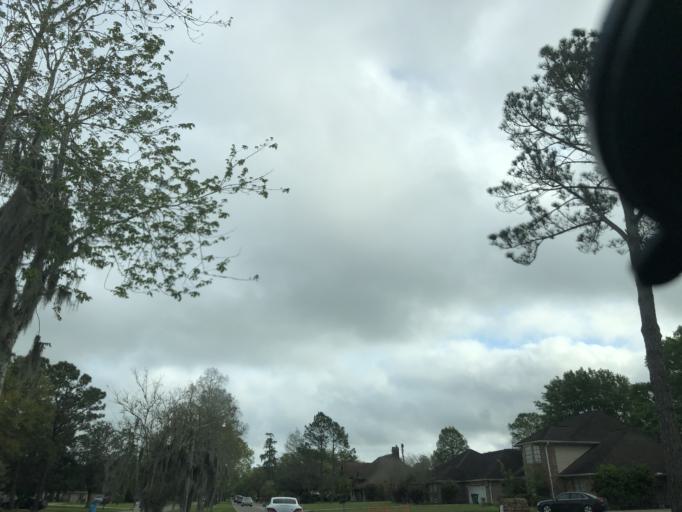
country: US
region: Louisiana
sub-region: Saint Charles Parish
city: New Sarpy
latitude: 29.9712
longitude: -90.3667
